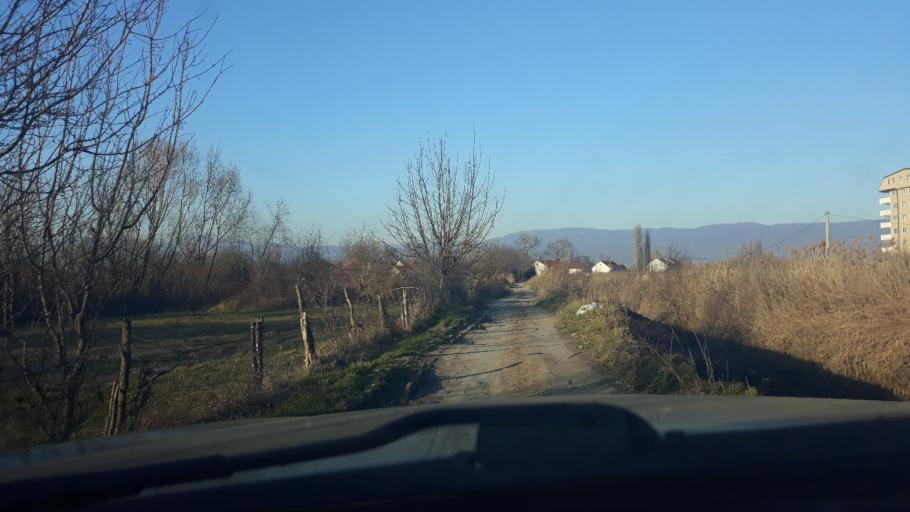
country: MK
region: Strumica
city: Strumica
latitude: 41.4432
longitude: 22.6268
